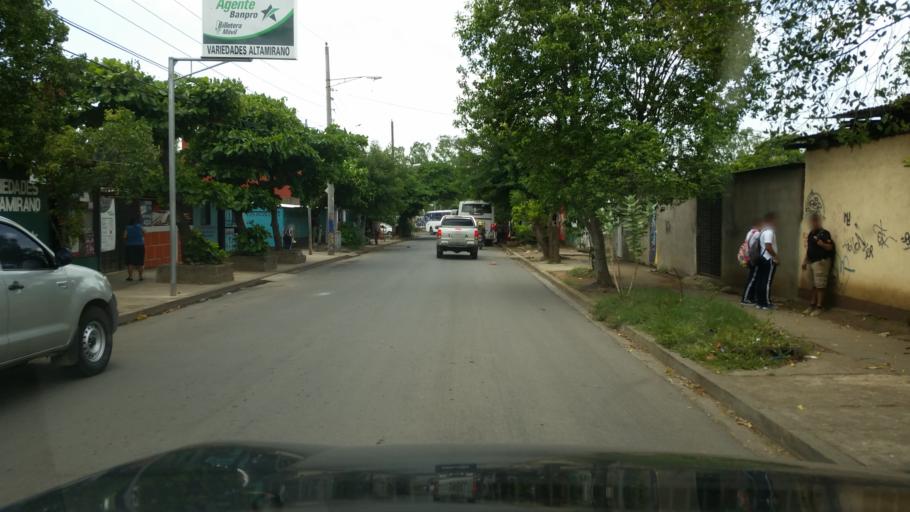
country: NI
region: Managua
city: Managua
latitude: 12.1383
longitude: -86.2091
